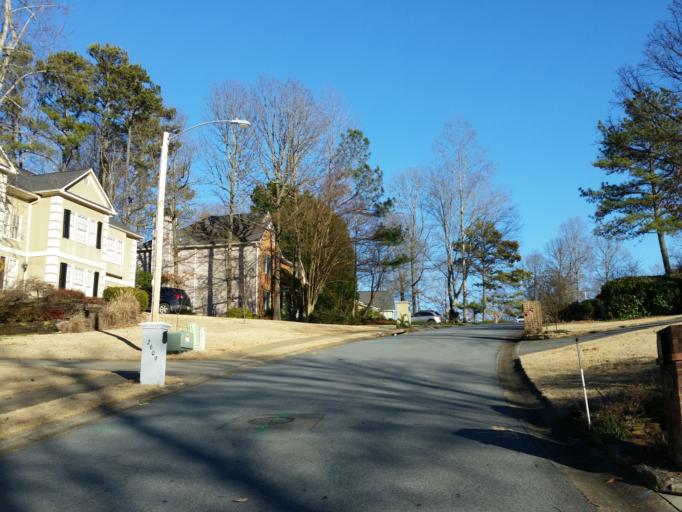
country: US
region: Georgia
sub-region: Cherokee County
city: Woodstock
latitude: 34.0550
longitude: -84.4790
